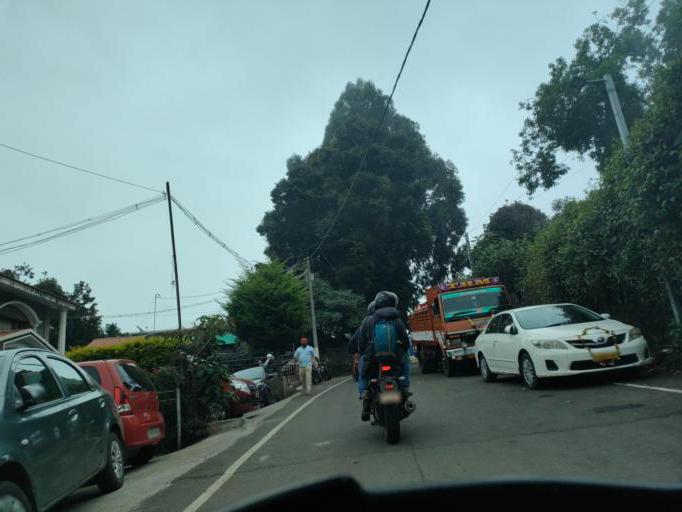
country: IN
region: Tamil Nadu
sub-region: Dindigul
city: Kodaikanal
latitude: 10.2386
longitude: 77.4851
